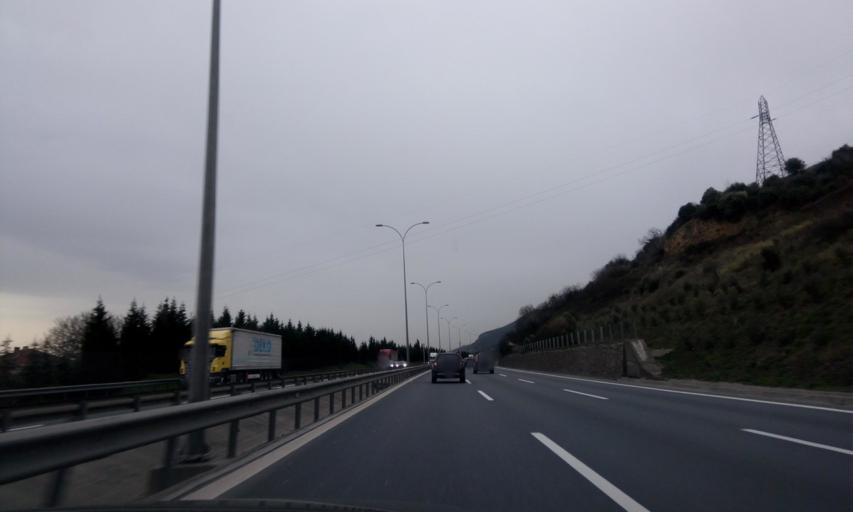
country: TR
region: Kocaeli
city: Ulasli
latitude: 40.7790
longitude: 29.7063
